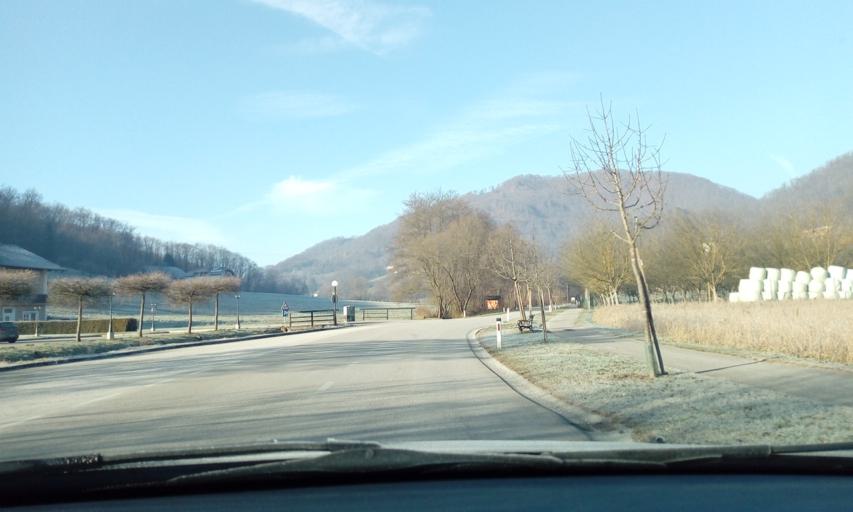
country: SI
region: Podcetrtek
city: Podcetrtek
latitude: 46.1453
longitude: 15.5777
